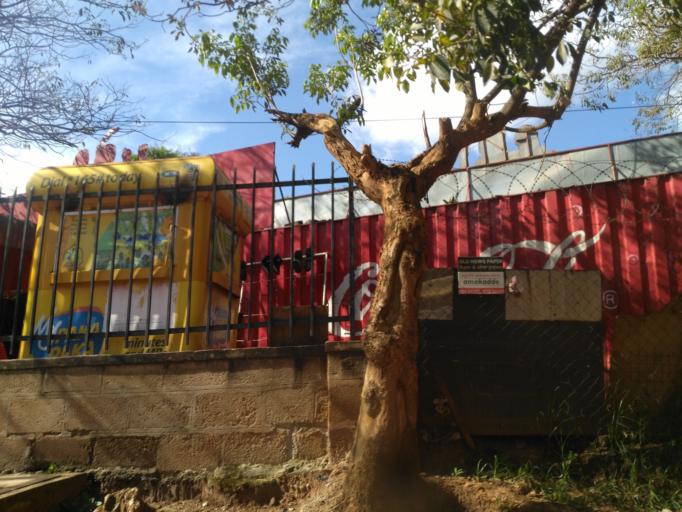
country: UG
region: Central Region
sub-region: Kampala District
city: Kampala
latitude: 0.3149
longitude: 32.5887
